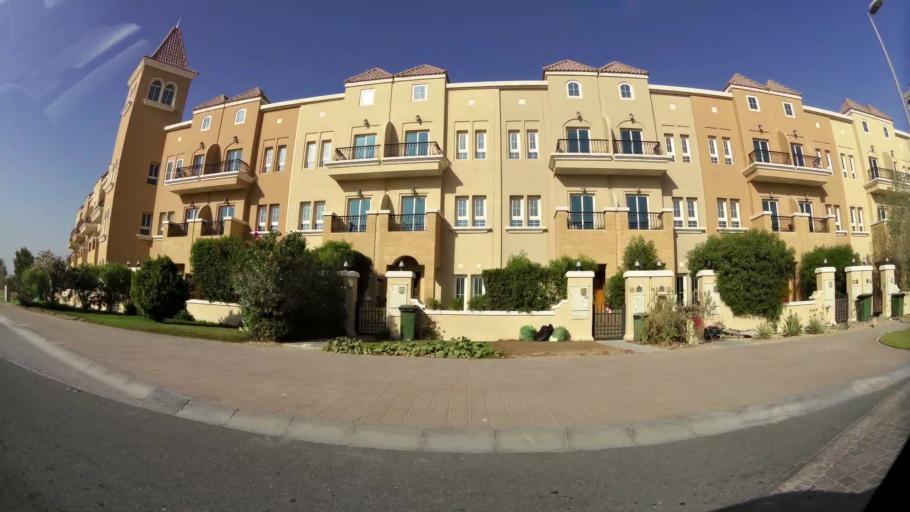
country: AE
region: Dubai
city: Dubai
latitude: 25.0576
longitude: 55.2194
